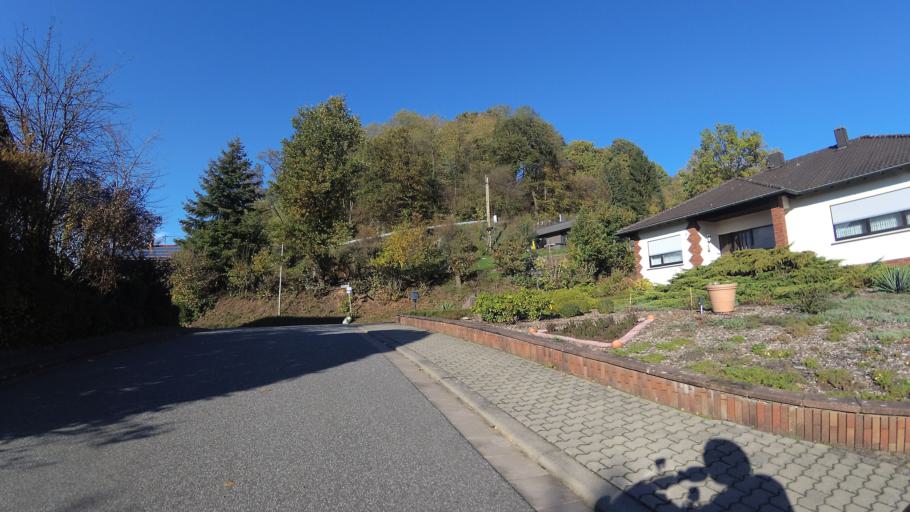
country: DE
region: Saarland
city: Losheim
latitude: 49.4873
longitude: 6.7883
